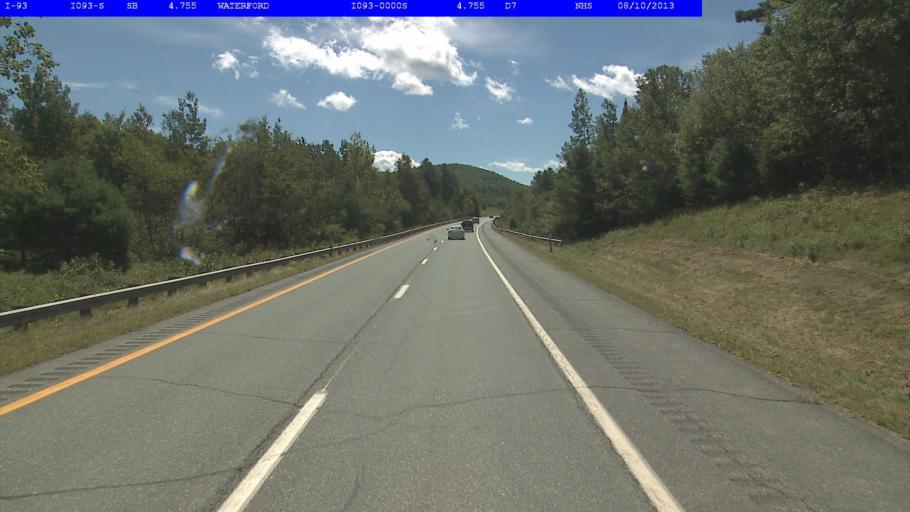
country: US
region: Vermont
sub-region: Caledonia County
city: Saint Johnsbury
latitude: 44.4041
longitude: -71.9195
